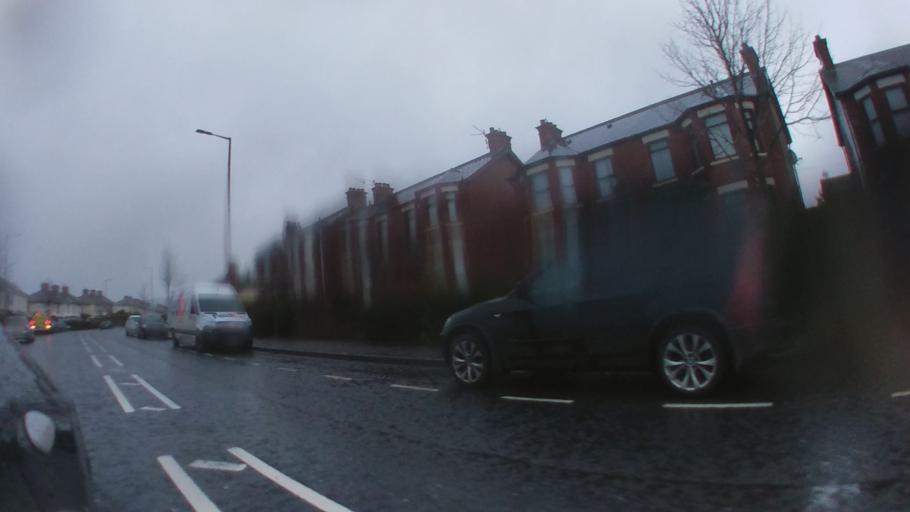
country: GB
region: Northern Ireland
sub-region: City of Belfast
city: Belfast
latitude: 54.6229
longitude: -5.9595
